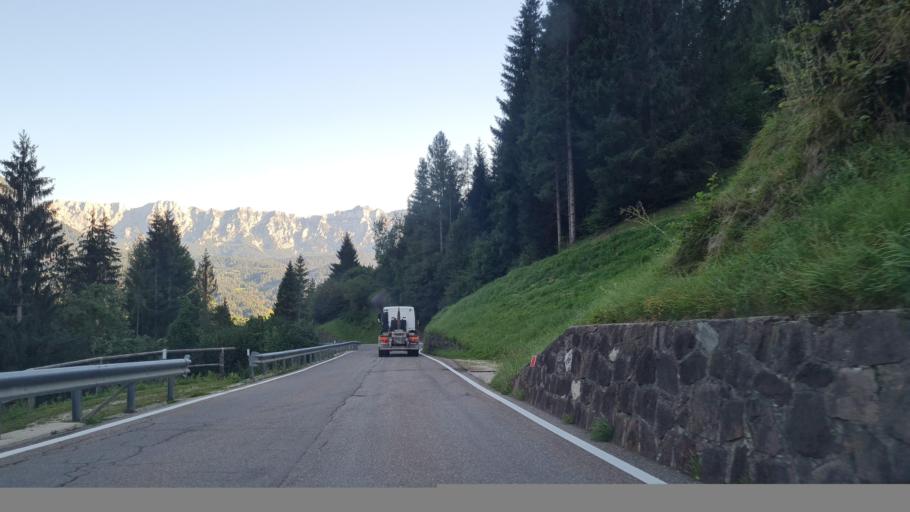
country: IT
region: Trentino-Alto Adige
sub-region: Provincia di Trento
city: Siror
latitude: 46.2023
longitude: 11.8203
